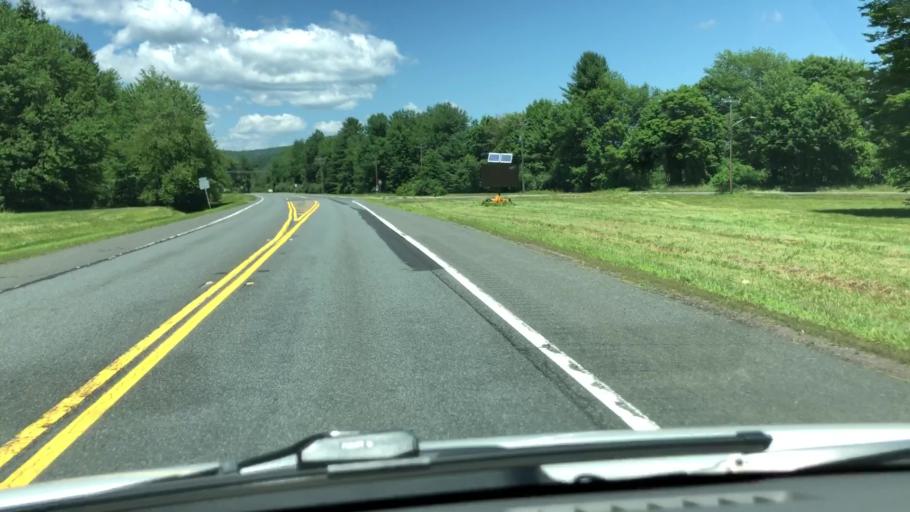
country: US
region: Massachusetts
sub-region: Hampshire County
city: North Amherst
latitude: 42.4207
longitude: -72.5370
